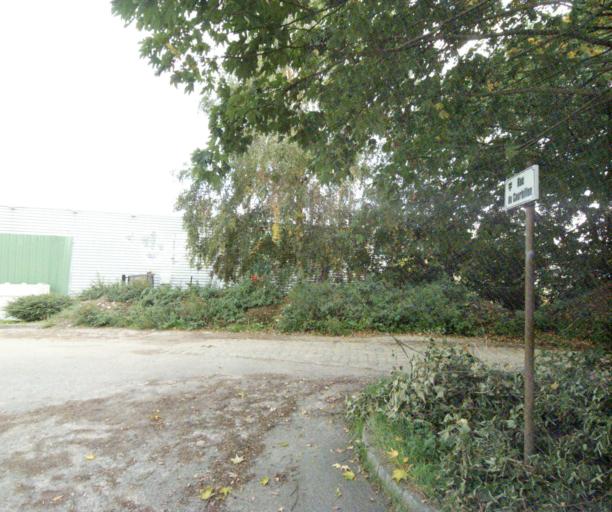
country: FR
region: Nord-Pas-de-Calais
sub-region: Departement du Nord
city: Vendeville
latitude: 50.5735
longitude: 3.0793
